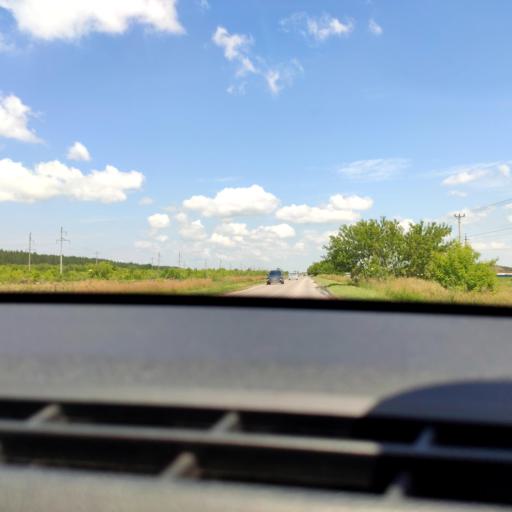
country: RU
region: Samara
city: Podstepki
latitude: 53.5345
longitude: 49.0860
